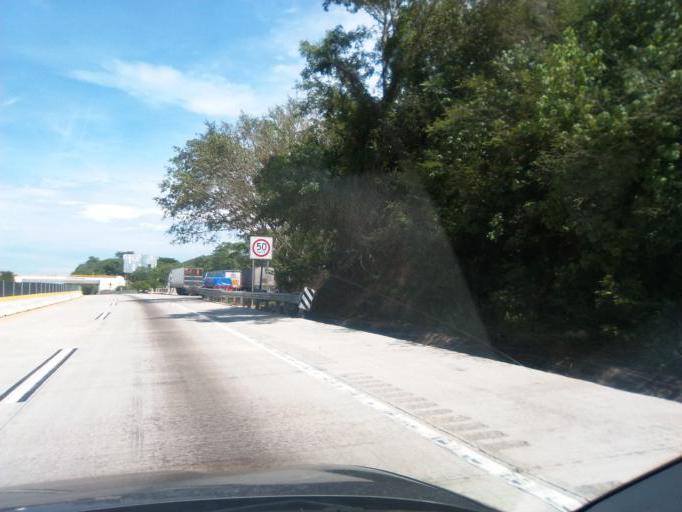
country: MX
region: Guerrero
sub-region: Acapulco de Juarez
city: Kilometro 30
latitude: 16.9622
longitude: -99.7380
